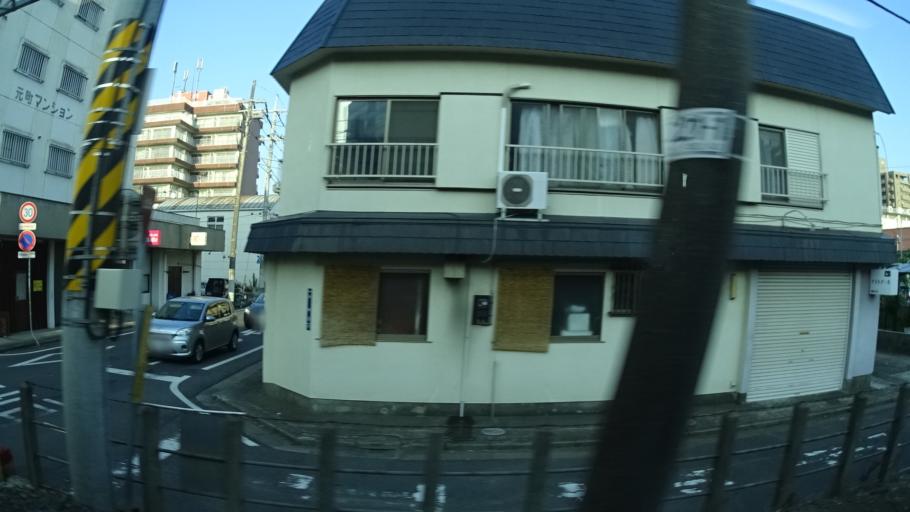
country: JP
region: Ibaraki
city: Hitachi-Naka
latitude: 36.3968
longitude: 140.5248
